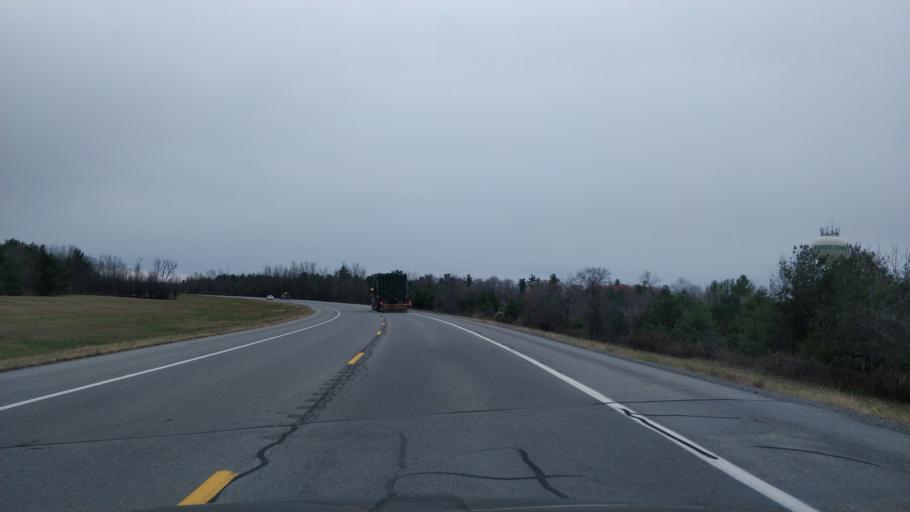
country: CA
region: Ontario
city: Brockville
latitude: 44.5904
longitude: -75.6404
